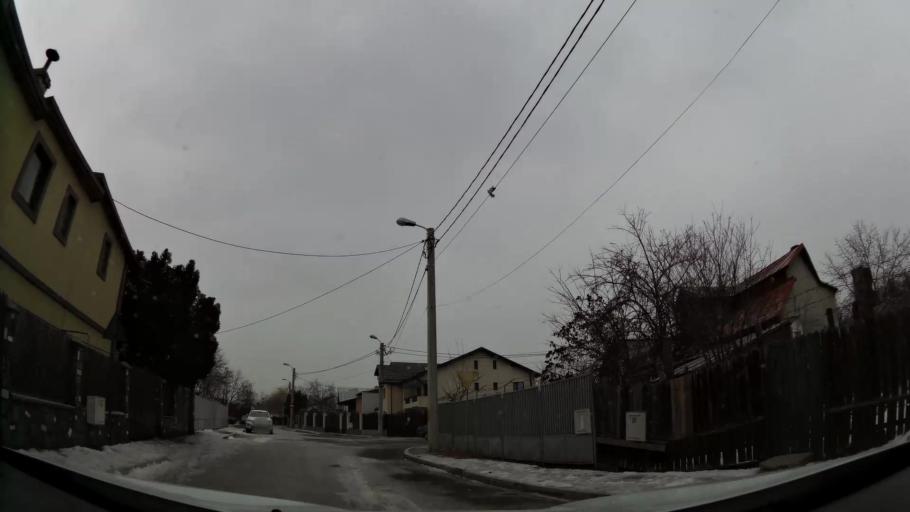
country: RO
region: Prahova
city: Ploiesti
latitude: 44.9403
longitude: 26.0435
